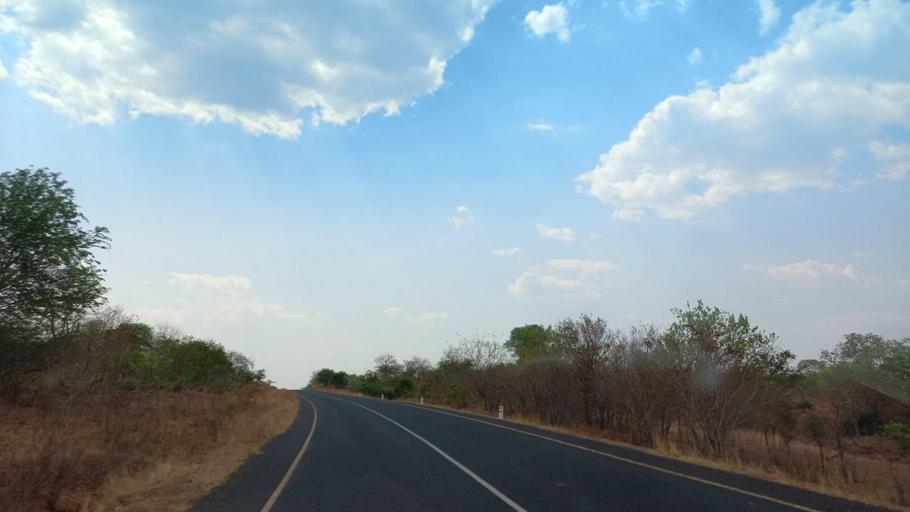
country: ZM
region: Lusaka
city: Luangwa
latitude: -15.2175
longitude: 30.2362
